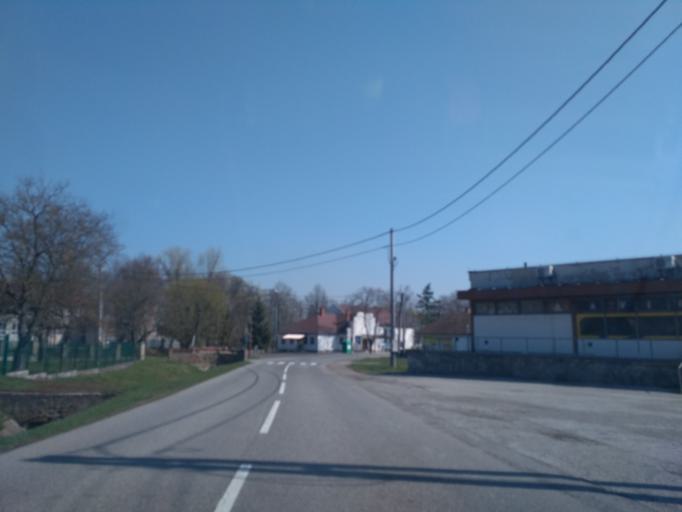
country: SK
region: Kosicky
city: Secovce
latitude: 48.7385
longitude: 21.6196
